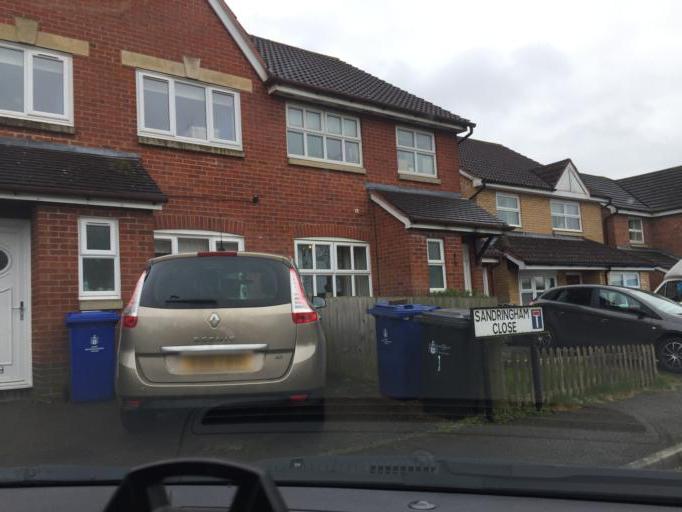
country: GB
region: England
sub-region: Northamptonshire
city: Brackley
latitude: 52.0322
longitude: -1.1539
